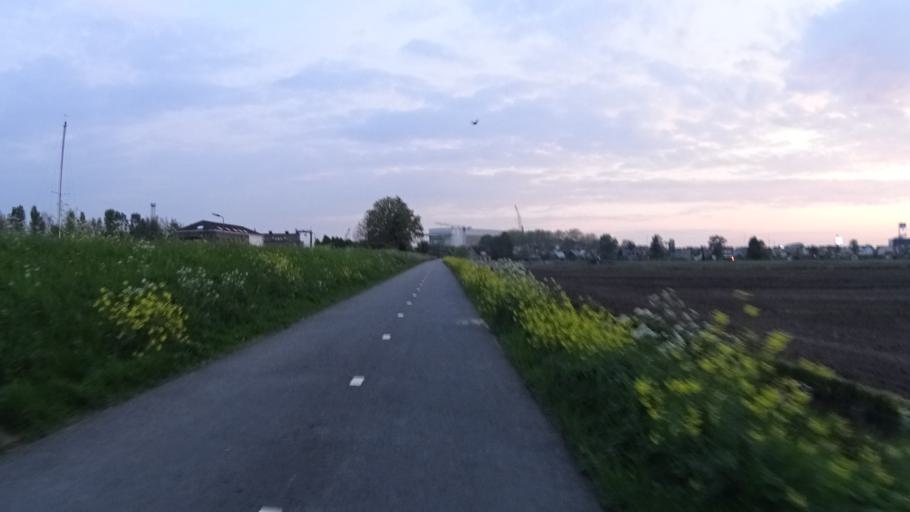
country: NL
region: South Holland
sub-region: Gemeente Hardinxveld-Giessendam
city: Neder-Hardinxveld
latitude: 51.8233
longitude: 4.8612
